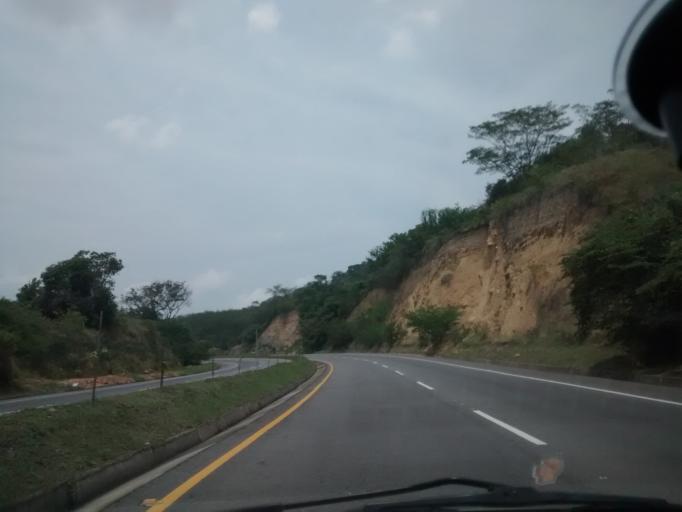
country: CO
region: Tolima
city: Espinal
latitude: 4.2155
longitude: -74.9509
